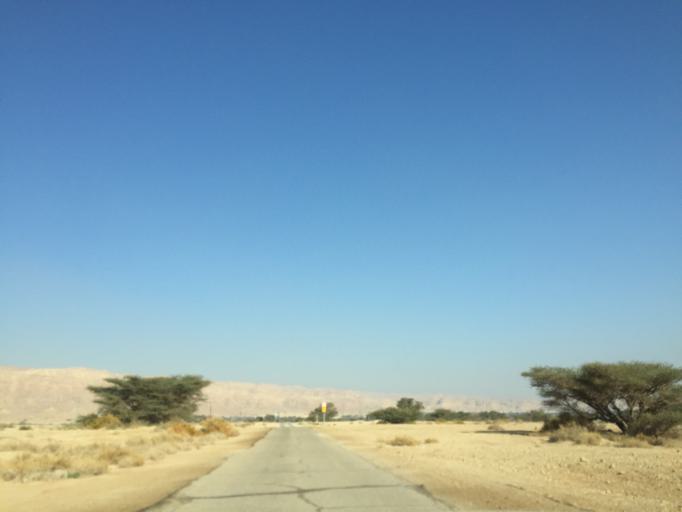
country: JO
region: Ma'an
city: Al Quwayrah
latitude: 29.8392
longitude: 35.0308
